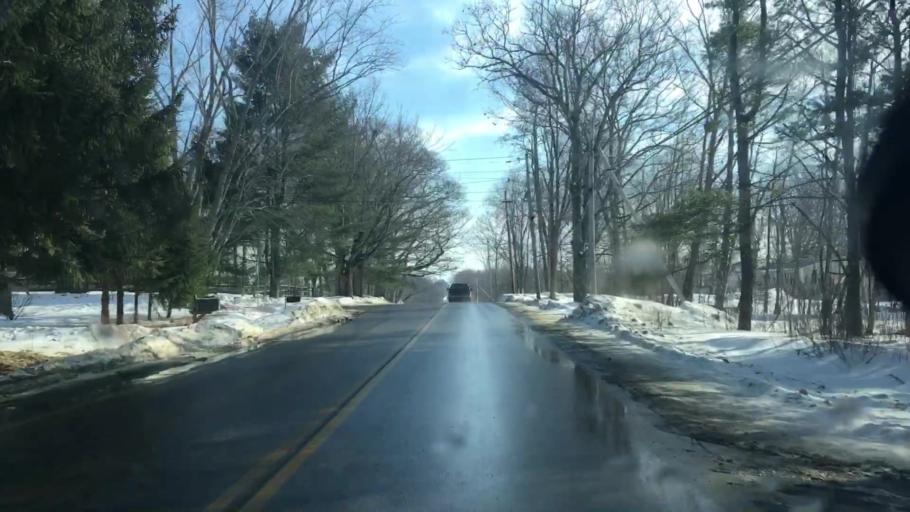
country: US
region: Maine
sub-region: Penobscot County
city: Bangor
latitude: 44.8463
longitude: -68.8373
